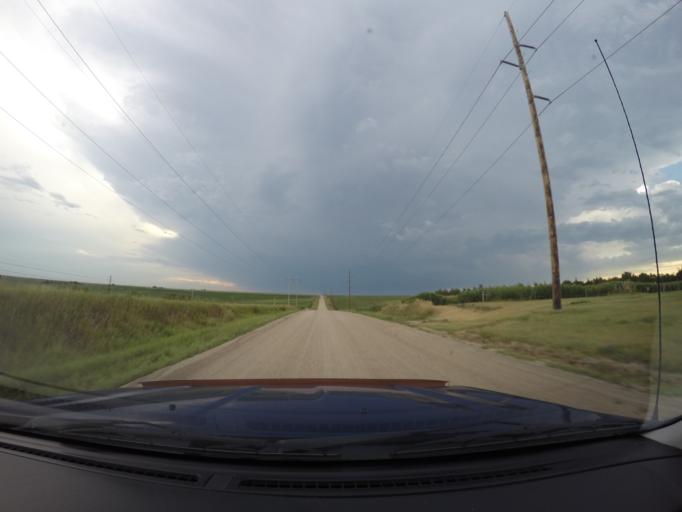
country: US
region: Nebraska
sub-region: Buffalo County
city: Kearney
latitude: 40.8445
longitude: -99.0856
